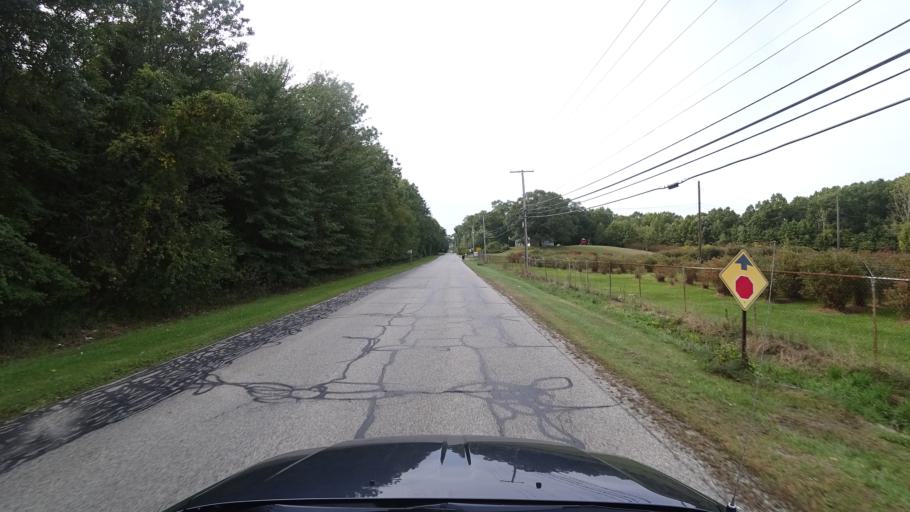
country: US
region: Indiana
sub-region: LaPorte County
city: Long Beach
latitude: 41.7386
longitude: -86.8328
